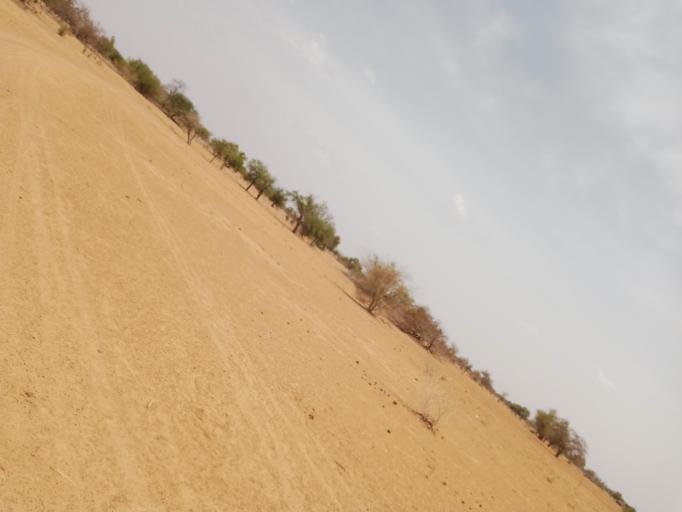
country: BF
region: Est
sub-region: Gnagna Province
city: Bogande
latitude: 13.0968
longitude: -0.0403
